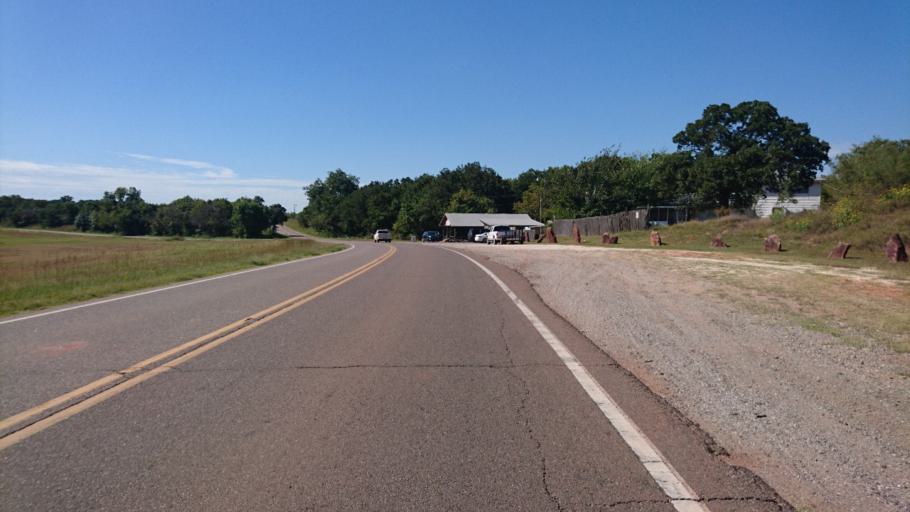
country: US
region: Oklahoma
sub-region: Oklahoma County
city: Luther
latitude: 35.6666
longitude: -97.2461
